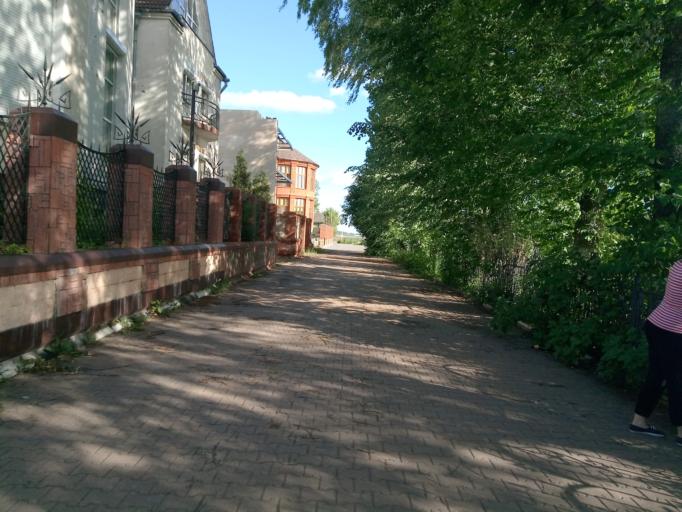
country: RU
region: Jaroslavl
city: Yaroslavl
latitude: 57.6355
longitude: 39.9041
